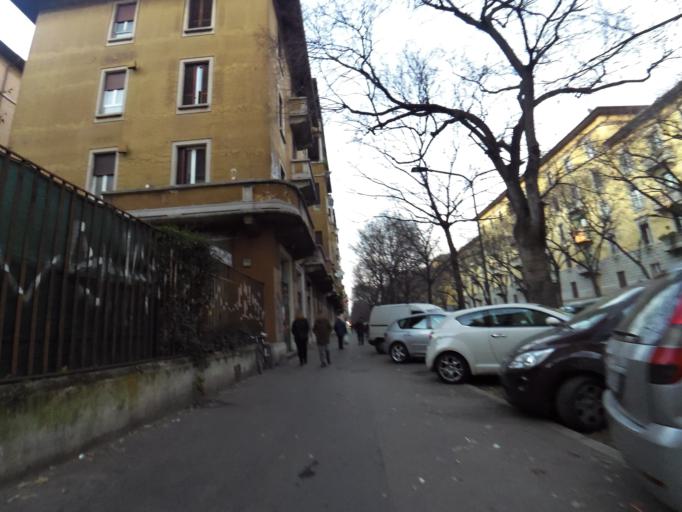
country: IT
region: Lombardy
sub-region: Citta metropolitana di Milano
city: Milano
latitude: 45.4626
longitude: 9.2146
